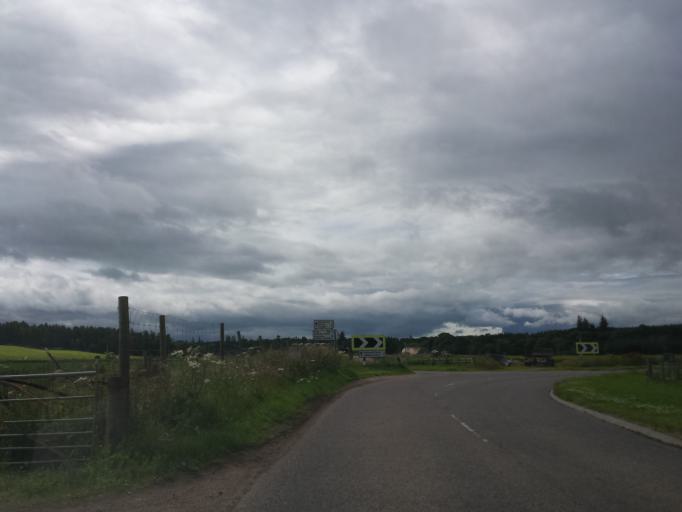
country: GB
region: Scotland
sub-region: Highland
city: Nairn
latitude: 57.5235
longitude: -3.9595
